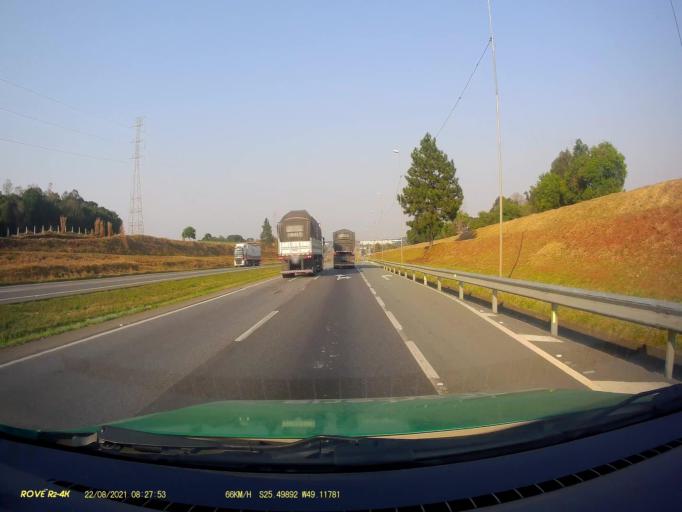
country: BR
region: Parana
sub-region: Piraquara
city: Piraquara
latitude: -25.4989
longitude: -49.1178
